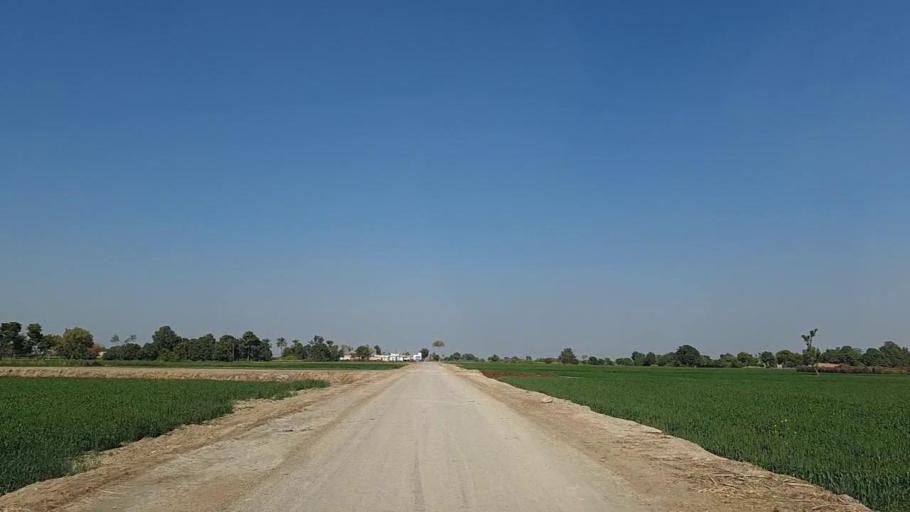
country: PK
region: Sindh
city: Nawabshah
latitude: 26.2560
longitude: 68.4515
